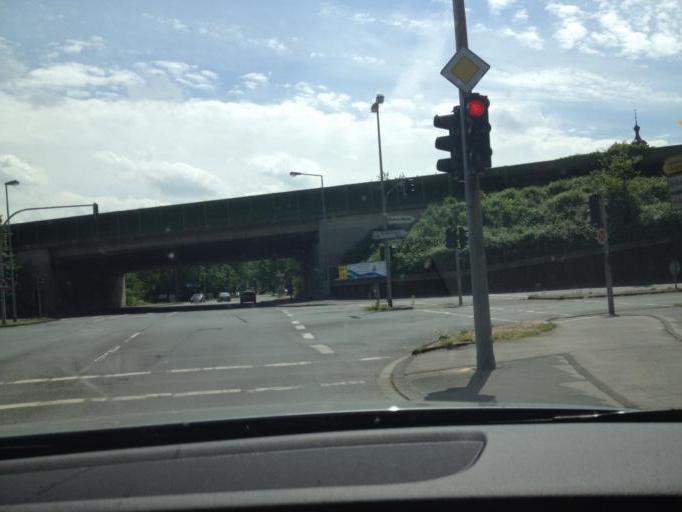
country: DE
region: North Rhine-Westphalia
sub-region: Regierungsbezirk Dusseldorf
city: Hochfeld
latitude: 51.3532
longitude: 6.7839
